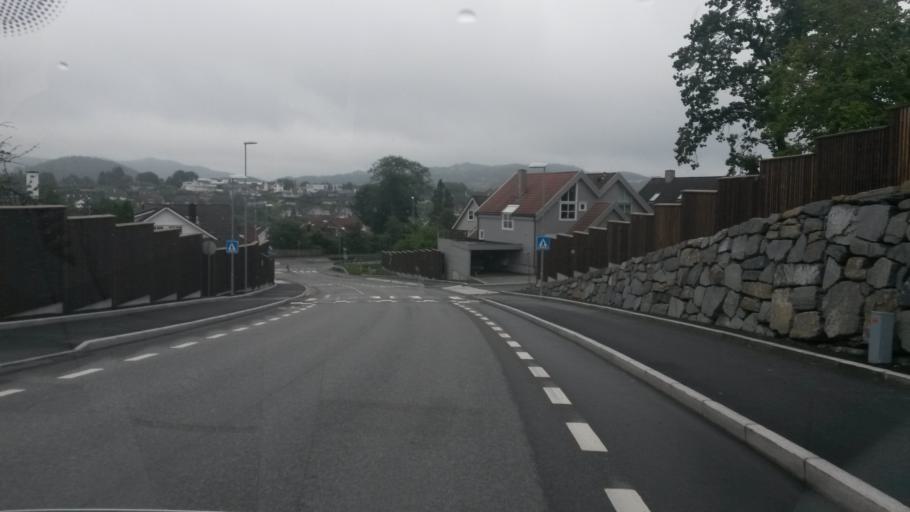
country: NO
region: Rogaland
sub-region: Sandnes
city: Sandnes
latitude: 58.8305
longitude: 5.7151
